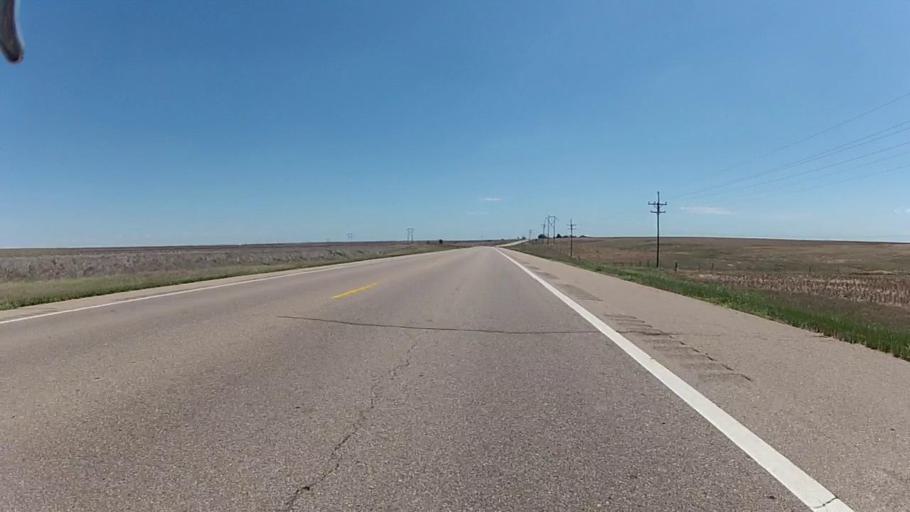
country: US
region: Kansas
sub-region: Ford County
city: Dodge City
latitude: 37.7043
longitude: -100.1399
